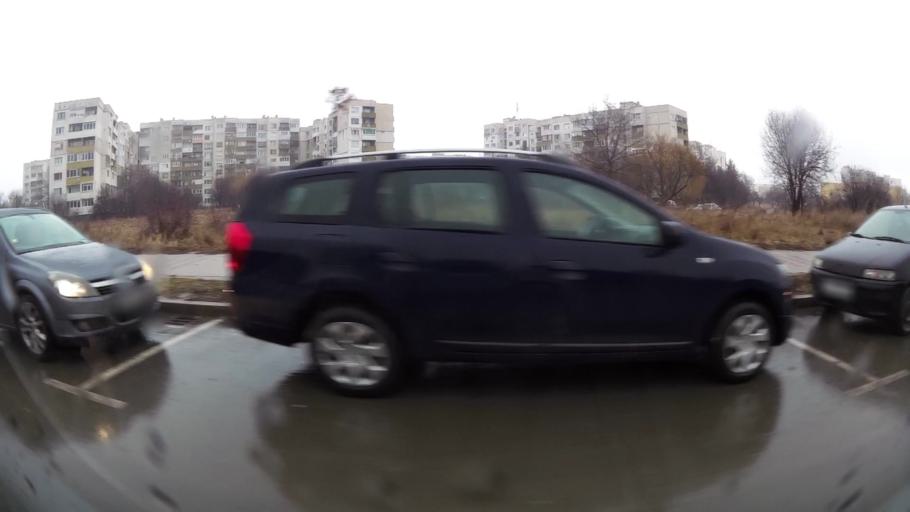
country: BG
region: Sofia-Capital
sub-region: Stolichna Obshtina
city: Sofia
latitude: 42.6515
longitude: 23.3967
